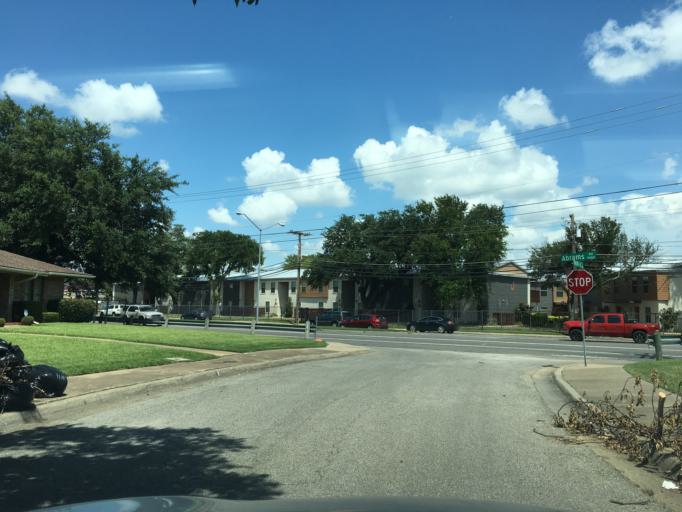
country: US
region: Texas
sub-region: Dallas County
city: Highland Park
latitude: 32.8545
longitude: -96.7530
